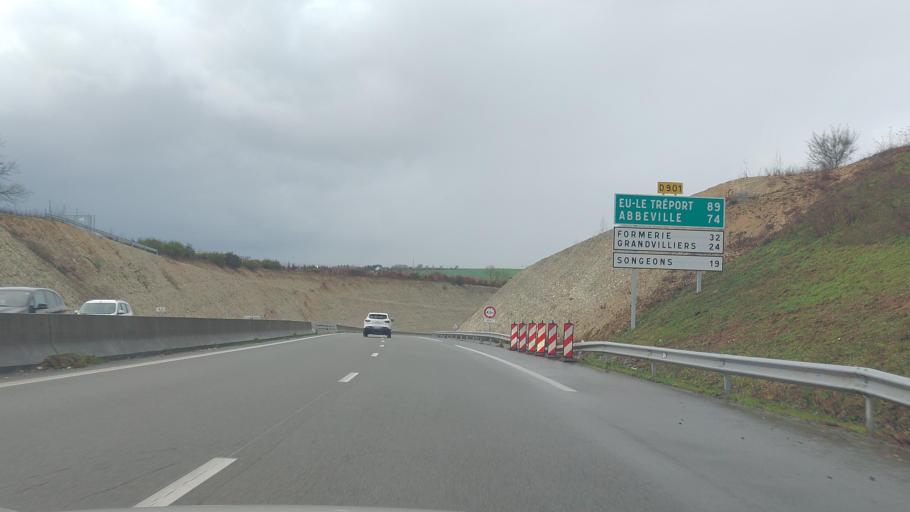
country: FR
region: Picardie
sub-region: Departement de l'Oise
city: Troissereux
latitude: 49.4781
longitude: 2.0666
